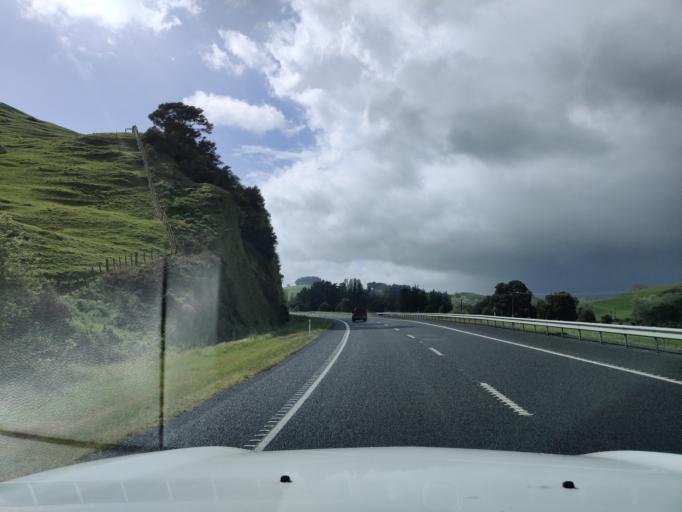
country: NZ
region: Waikato
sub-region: Matamata-Piako District
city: Matamata
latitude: -37.9528
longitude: 175.6770
